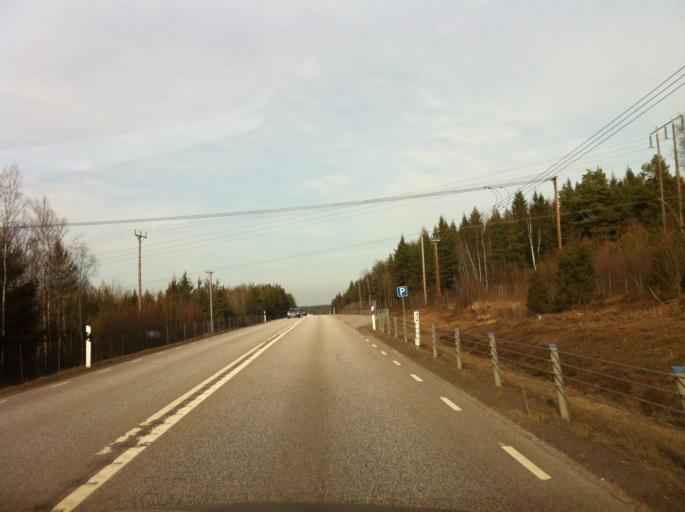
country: SE
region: Vaestra Goetaland
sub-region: Gullspangs Kommun
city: Gullspang
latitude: 58.9521
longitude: 14.0539
